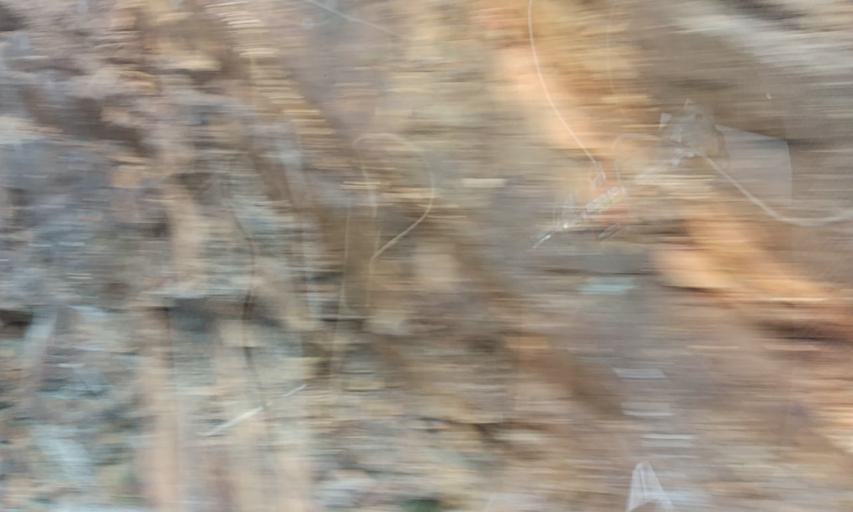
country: ES
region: Extremadura
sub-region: Provincia de Caceres
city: Acebo
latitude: 40.2027
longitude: -6.6762
